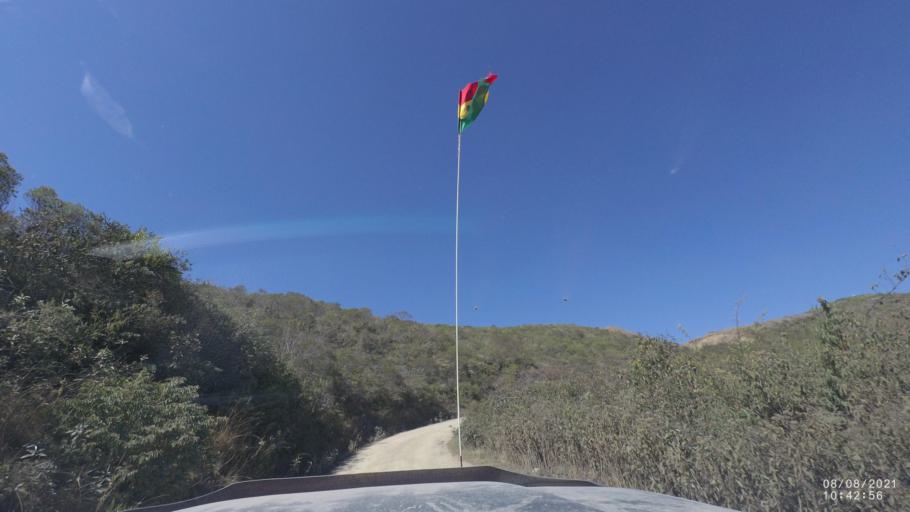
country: BO
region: La Paz
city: Quime
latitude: -16.7024
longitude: -66.7212
